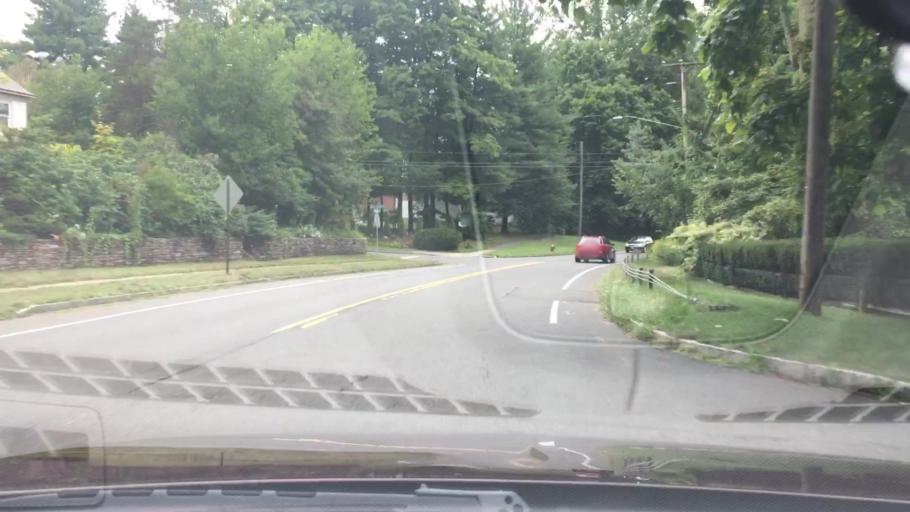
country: US
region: Connecticut
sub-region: Hartford County
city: West Hartford
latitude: 41.7622
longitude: -72.7653
